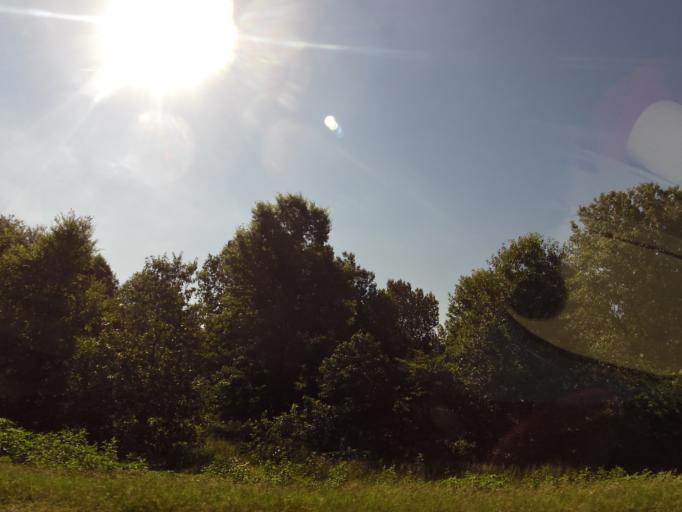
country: US
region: Arkansas
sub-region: Clay County
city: Corning
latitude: 36.4008
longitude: -90.5085
